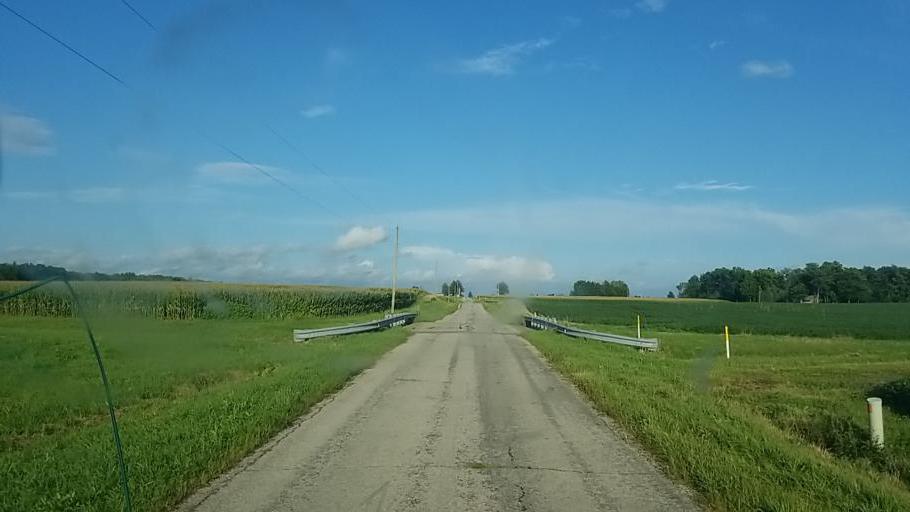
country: US
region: Ohio
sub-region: Crawford County
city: Bucyrus
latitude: 40.7396
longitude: -82.9582
